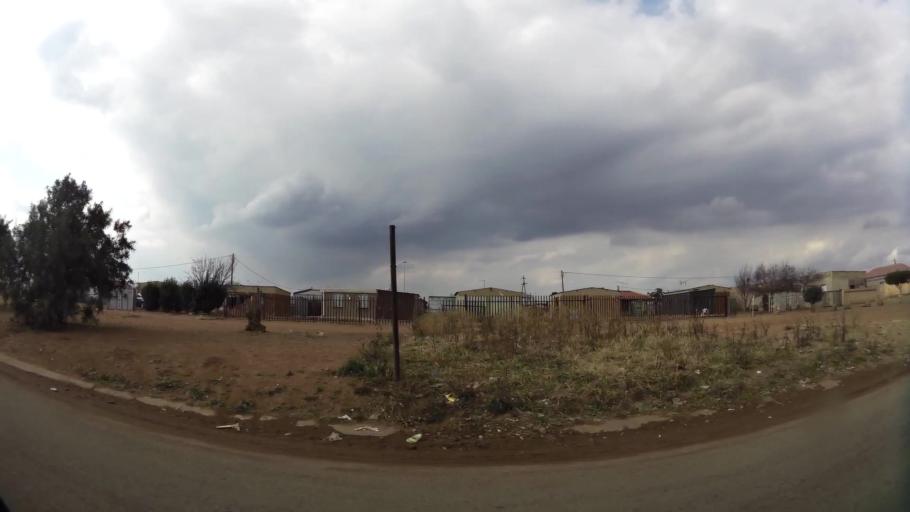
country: ZA
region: Gauteng
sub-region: Sedibeng District Municipality
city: Vanderbijlpark
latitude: -26.6805
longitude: 27.7809
